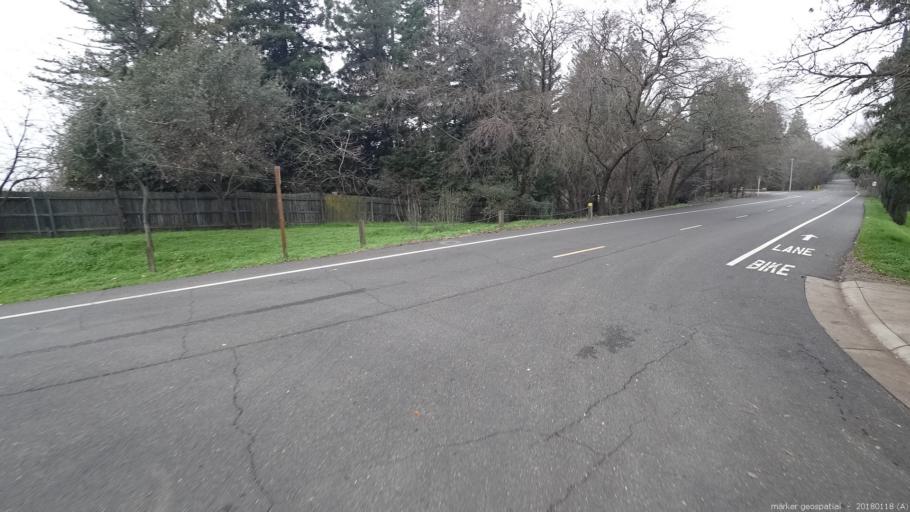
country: US
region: California
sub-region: Sacramento County
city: Rancho Cordova
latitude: 38.5843
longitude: -121.3232
